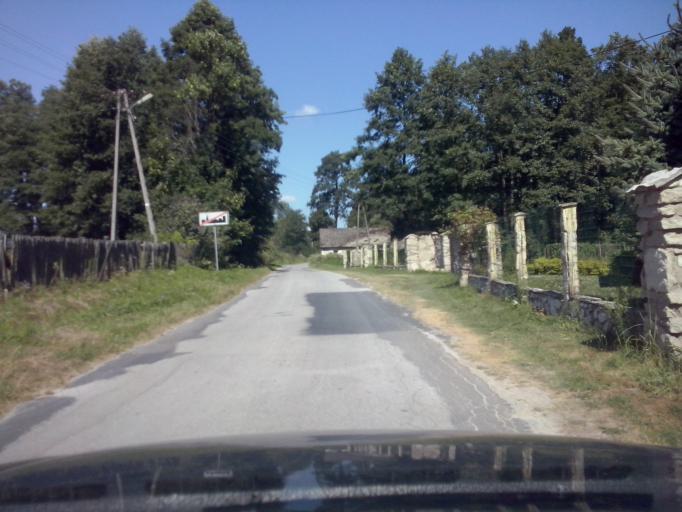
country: PL
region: Swietokrzyskie
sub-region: Powiat buski
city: Gnojno
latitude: 50.6110
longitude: 20.8904
